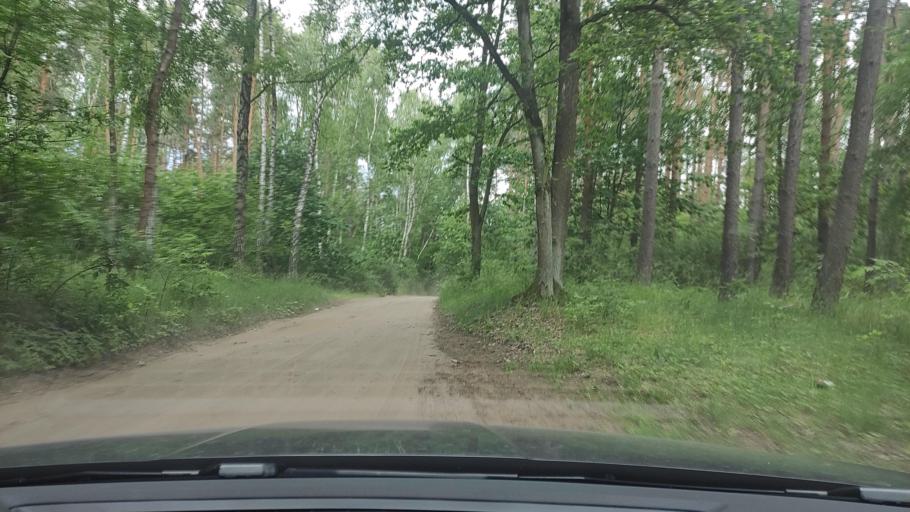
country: PL
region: Greater Poland Voivodeship
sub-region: Powiat poznanski
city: Pobiedziska
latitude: 52.5023
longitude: 17.2035
